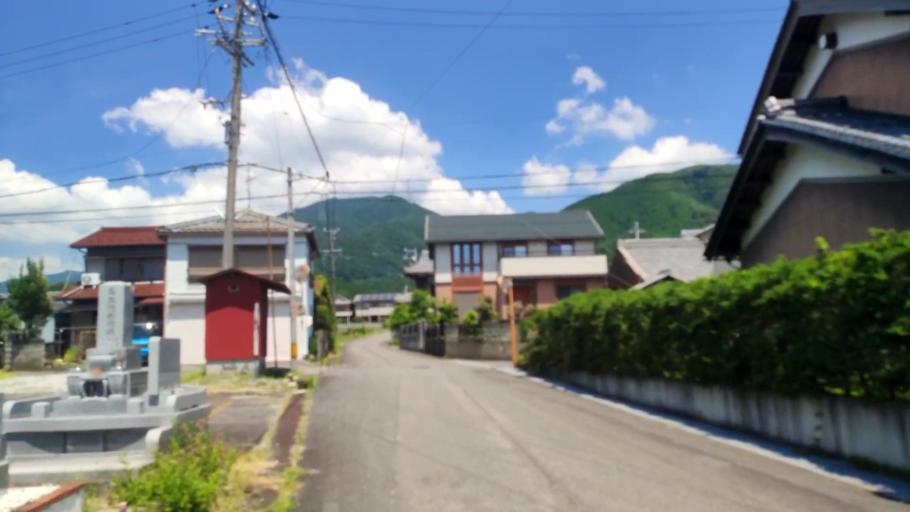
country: JP
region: Gifu
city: Tarui
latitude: 35.3677
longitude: 136.4631
